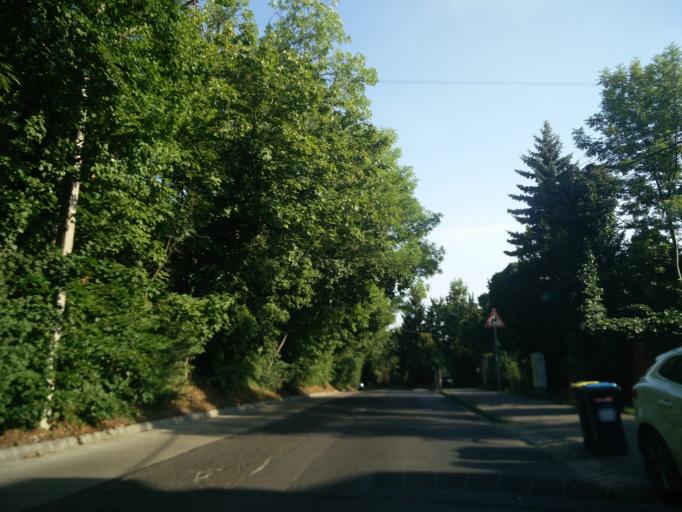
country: HU
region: Budapest
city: Budapest XII. keruelet
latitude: 47.5052
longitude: 18.9824
